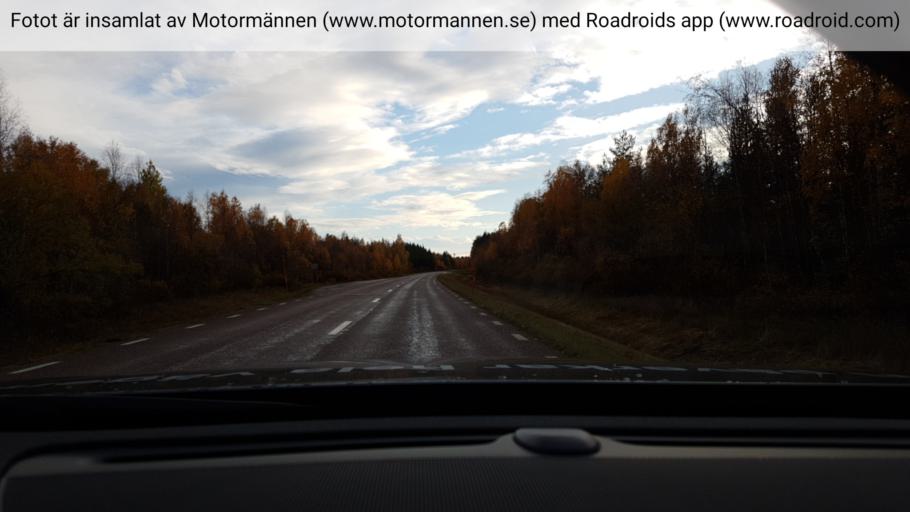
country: SE
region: Norrbotten
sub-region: Pajala Kommun
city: Pajala
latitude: 67.1509
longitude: 22.6272
